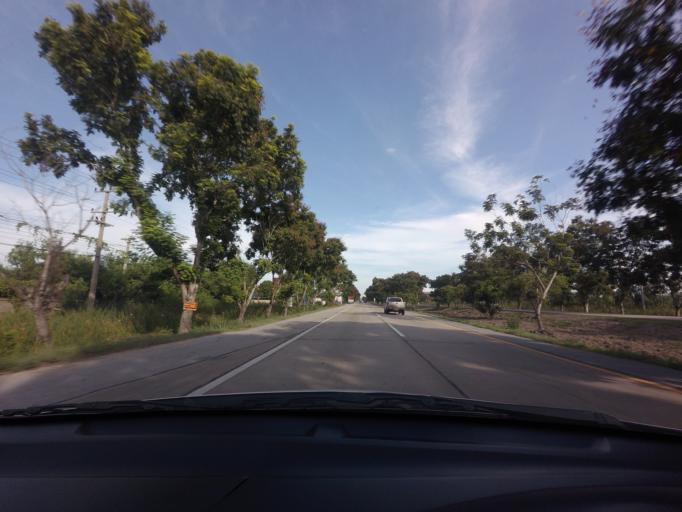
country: TH
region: Phra Nakhon Si Ayutthaya
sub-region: Amphoe Bang Sai
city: Bang Sai
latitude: 14.2623
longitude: 100.2554
